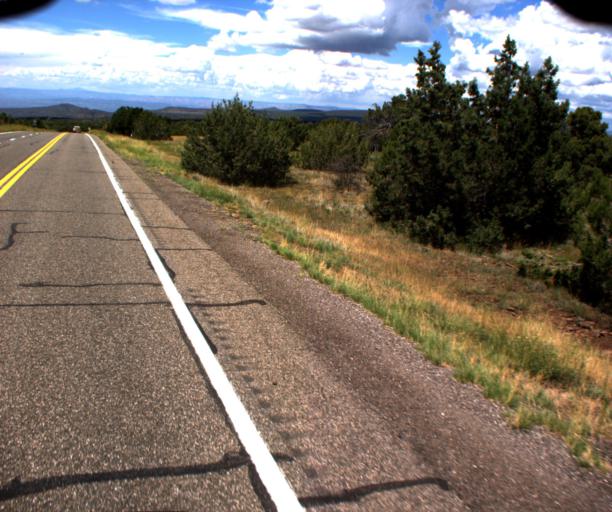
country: US
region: Arizona
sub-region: Gila County
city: Pine
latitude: 34.4890
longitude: -111.6250
